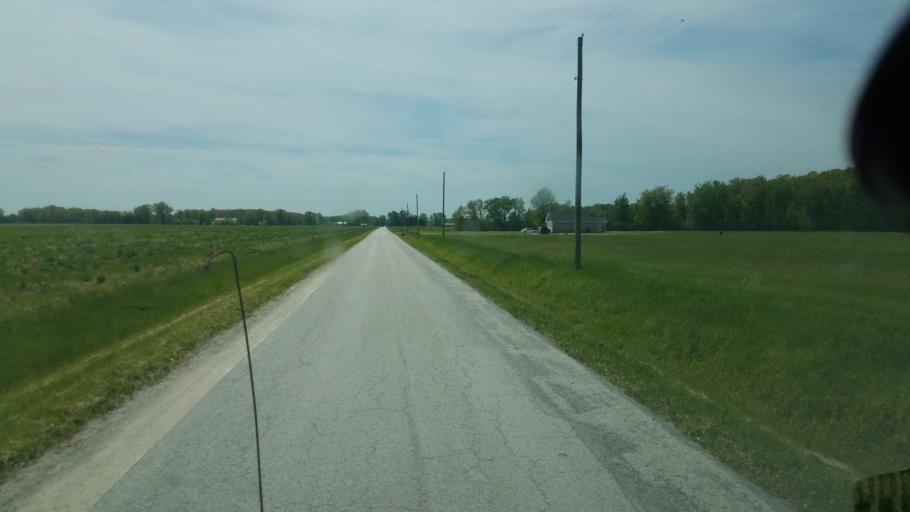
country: US
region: Ohio
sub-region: Ottawa County
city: Oak Harbor
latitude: 41.4932
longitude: -83.1643
